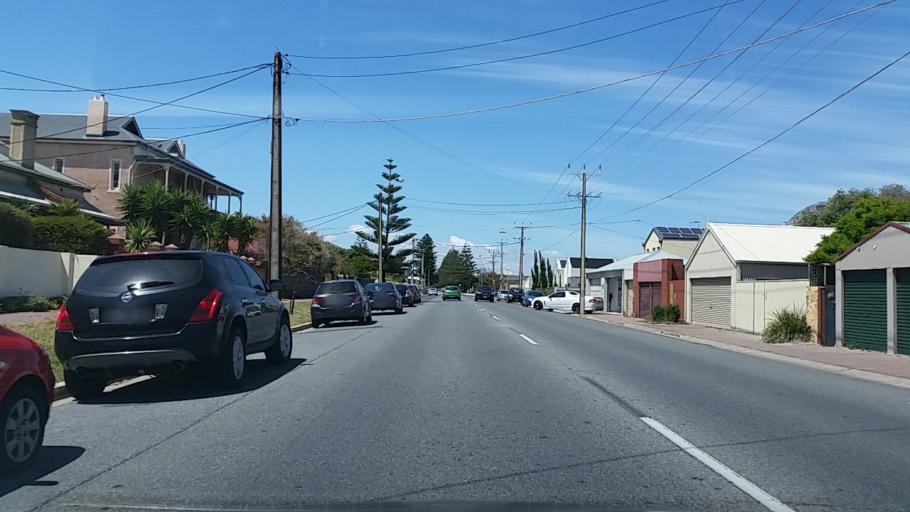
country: AU
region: South Australia
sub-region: Charles Sturt
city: Henley Beach
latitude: -34.9236
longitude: 138.4955
